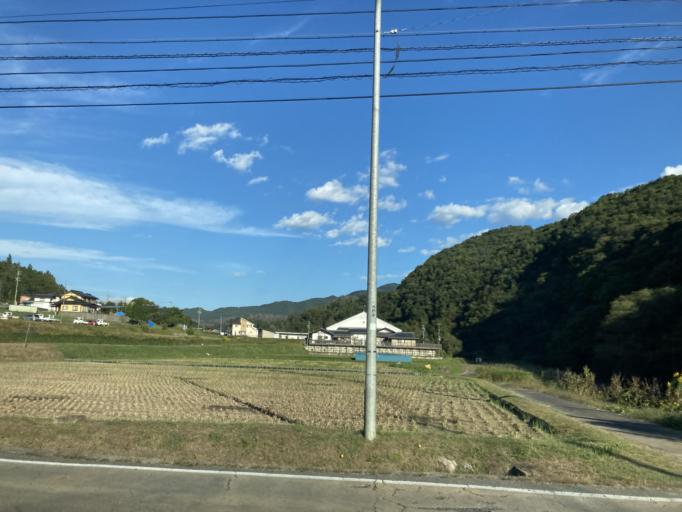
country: JP
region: Nagano
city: Omachi
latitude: 36.4381
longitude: 138.0085
